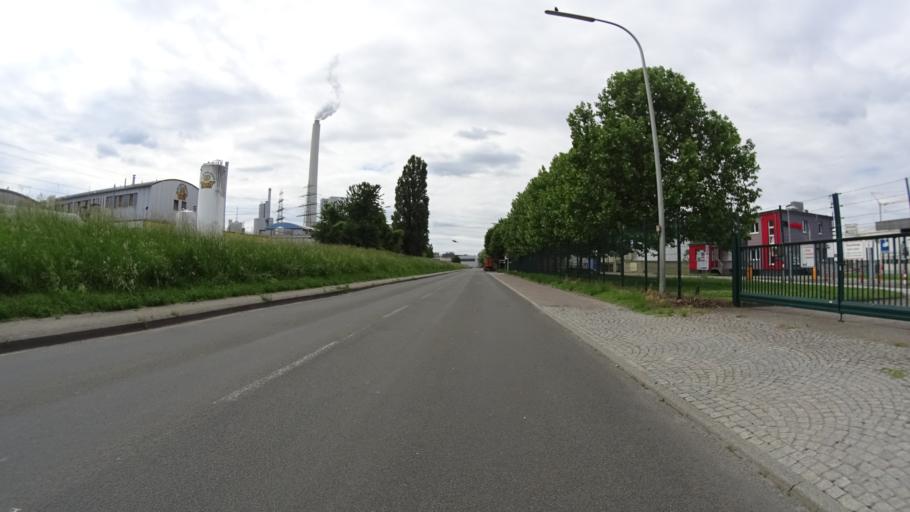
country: DE
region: Baden-Wuerttemberg
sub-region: Karlsruhe Region
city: Rheinstetten
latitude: 49.0117
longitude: 8.3171
